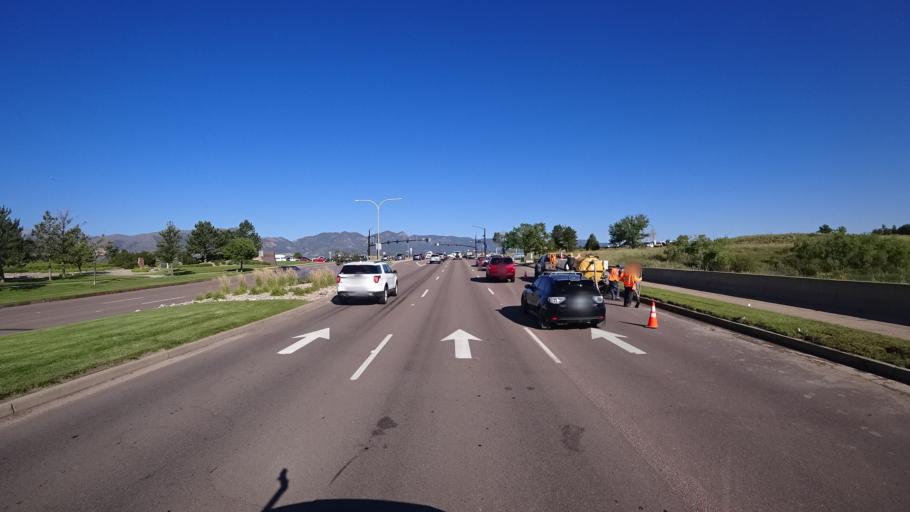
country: US
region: Colorado
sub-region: El Paso County
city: Air Force Academy
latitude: 38.9656
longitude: -104.7972
